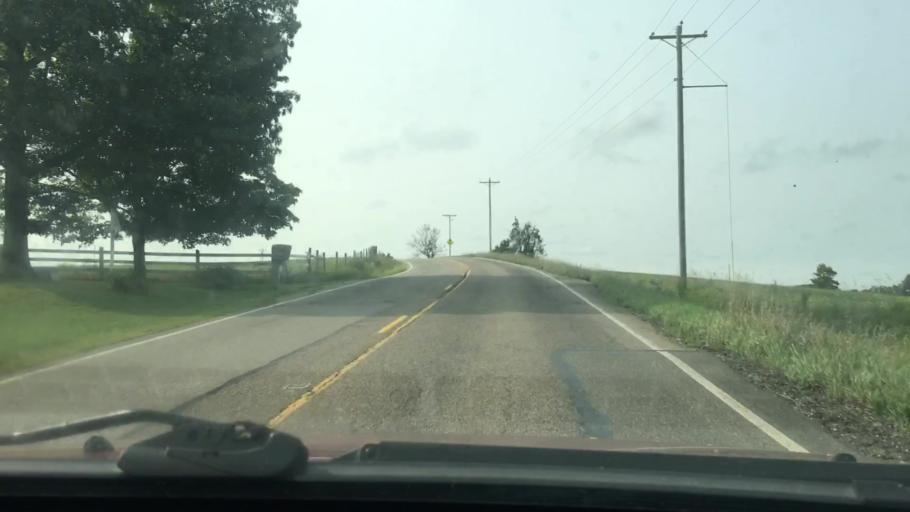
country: US
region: Ohio
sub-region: Belmont County
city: Barnesville
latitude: 40.1544
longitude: -81.2361
